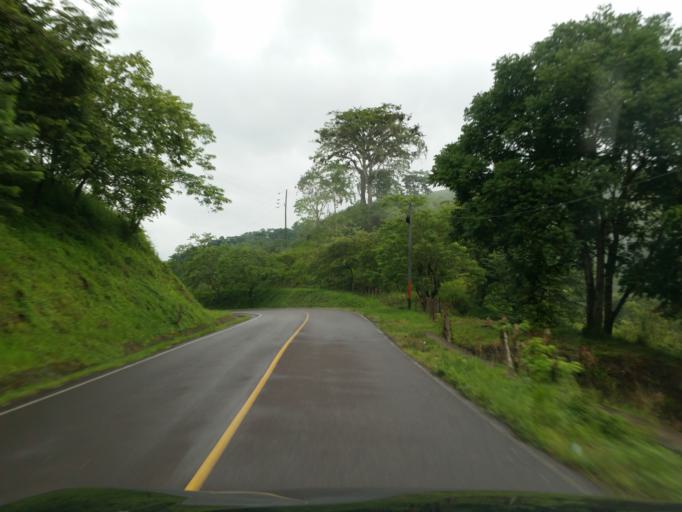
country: NI
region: Matagalpa
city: San Ramon
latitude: 13.0247
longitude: -85.7829
